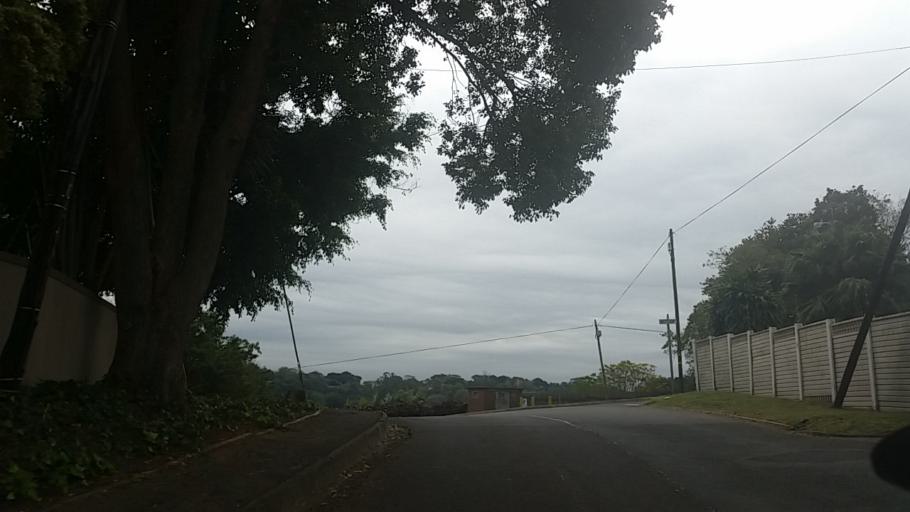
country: ZA
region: KwaZulu-Natal
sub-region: eThekwini Metropolitan Municipality
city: Berea
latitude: -29.8438
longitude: 30.9303
